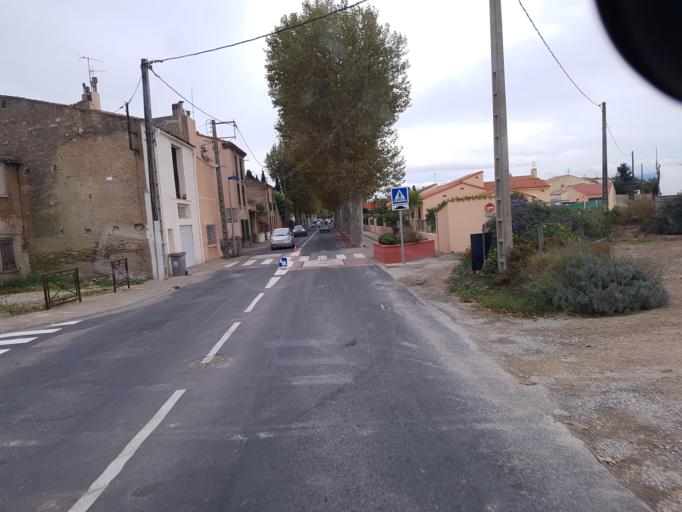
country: FR
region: Languedoc-Roussillon
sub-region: Departement des Pyrenees-Orientales
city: Torreilles
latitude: 42.7613
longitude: 2.9888
